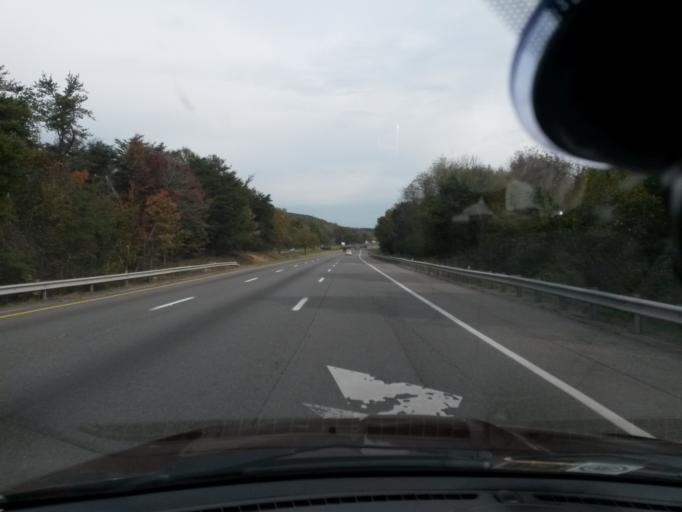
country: US
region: Virginia
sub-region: Roanoke County
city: Hollins
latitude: 37.3437
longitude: -79.9933
